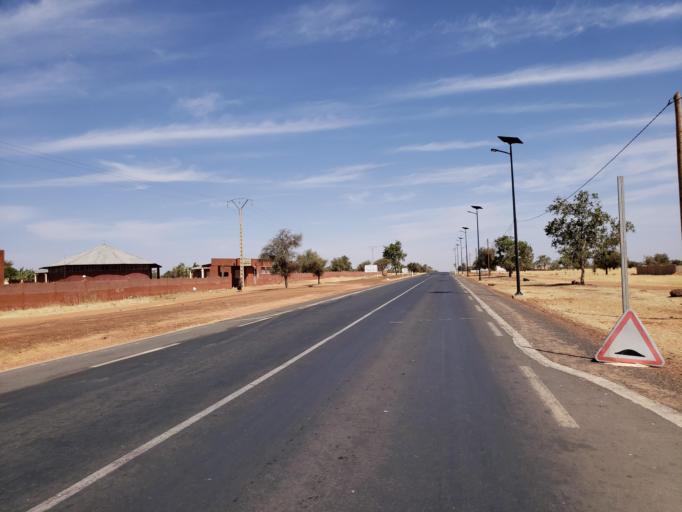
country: SN
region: Matam
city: Ranerou
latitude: 15.3038
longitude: -13.9524
